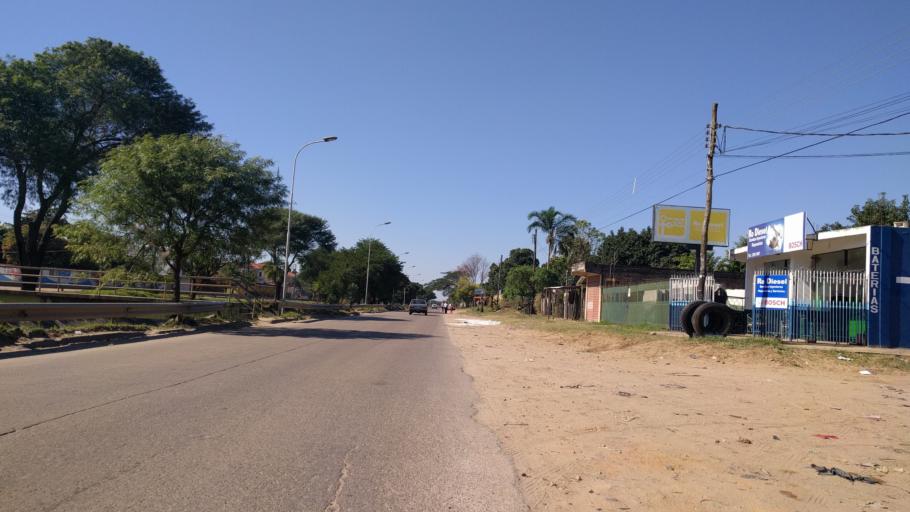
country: BO
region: Santa Cruz
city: Santa Cruz de la Sierra
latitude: -17.8180
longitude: -63.2253
